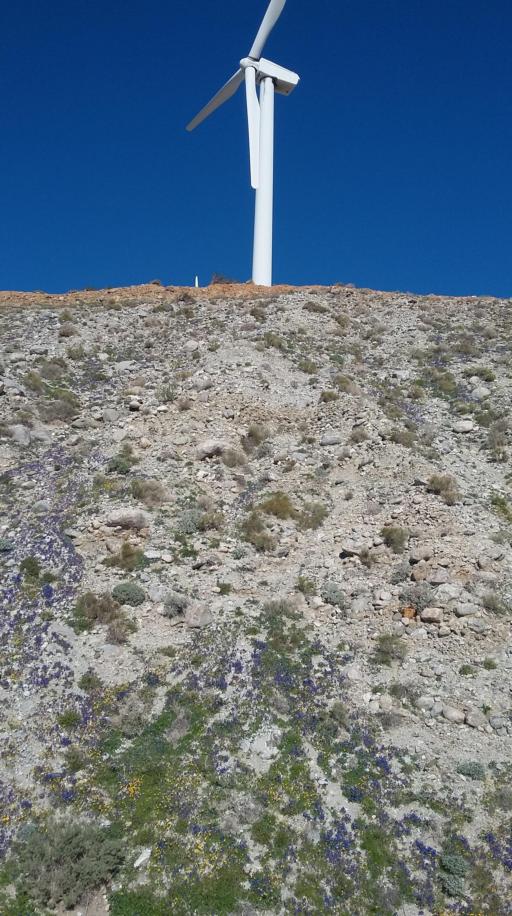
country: US
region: California
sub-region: Riverside County
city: Garnet
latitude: 33.9240
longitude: -116.6323
